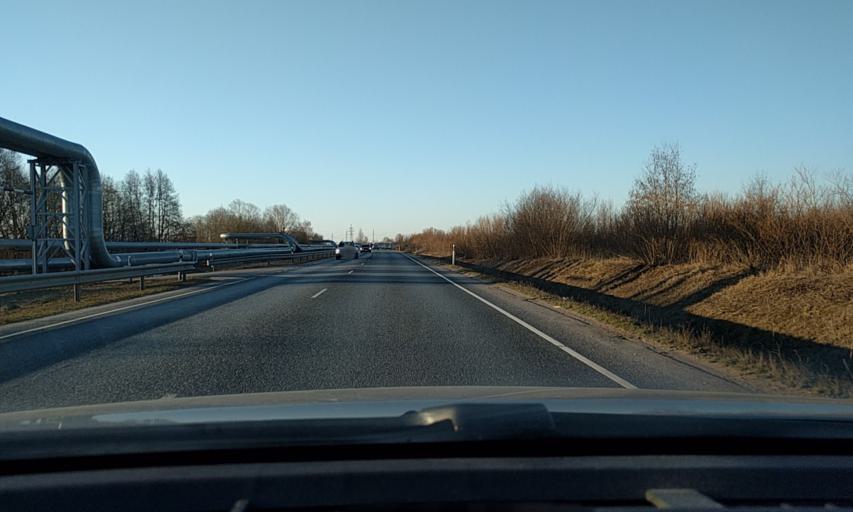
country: EE
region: Harju
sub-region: Maardu linn
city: Maardu
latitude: 59.4756
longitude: 24.9813
